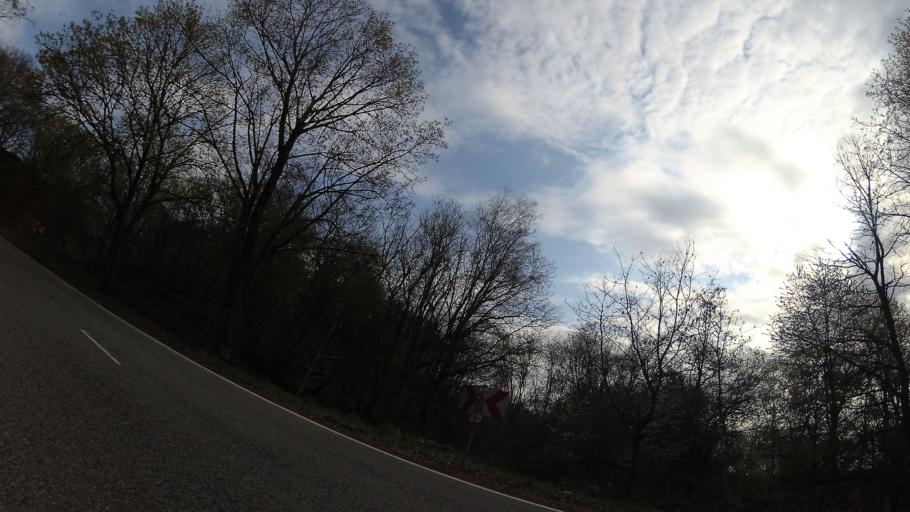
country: DE
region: Rheinland-Pfalz
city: Herschweiler-Pettersheim
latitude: 49.4818
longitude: 7.3617
